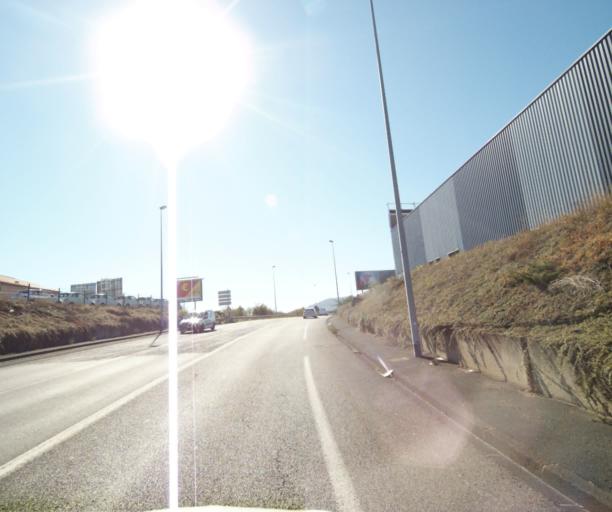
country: FR
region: Auvergne
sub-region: Departement du Puy-de-Dome
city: Aubiere
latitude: 45.7792
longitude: 3.1315
